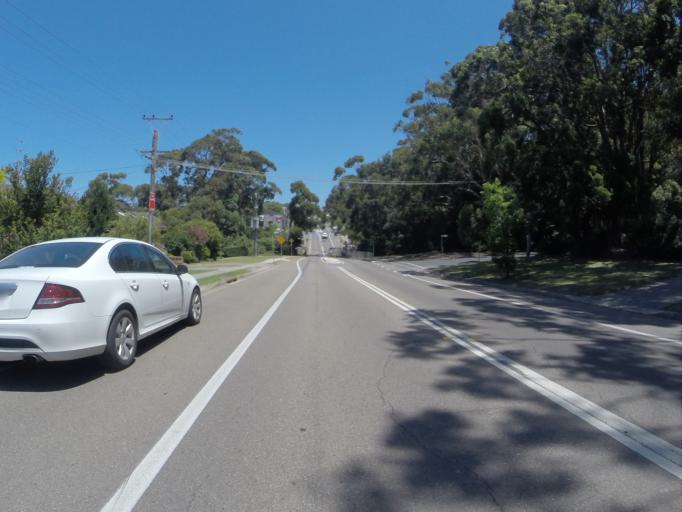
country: AU
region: New South Wales
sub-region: Shoalhaven Shire
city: Ulladulla
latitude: -35.3542
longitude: 150.4724
